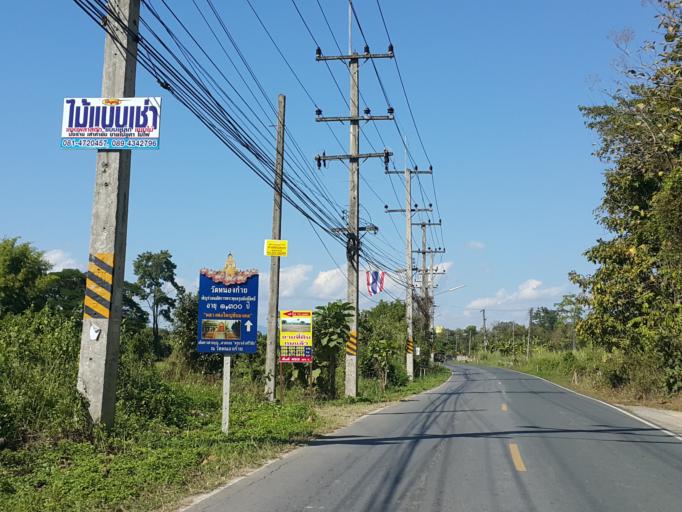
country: TH
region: Chiang Mai
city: San Sai
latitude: 18.9453
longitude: 98.9274
